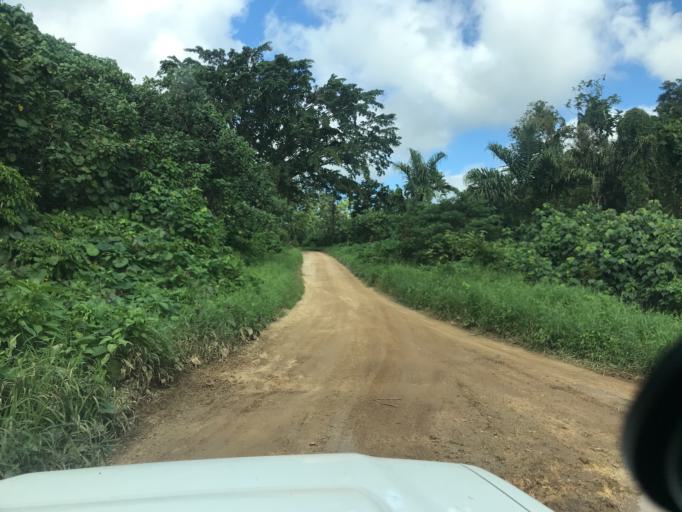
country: VU
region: Sanma
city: Luganville
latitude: -15.4733
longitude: 167.0777
